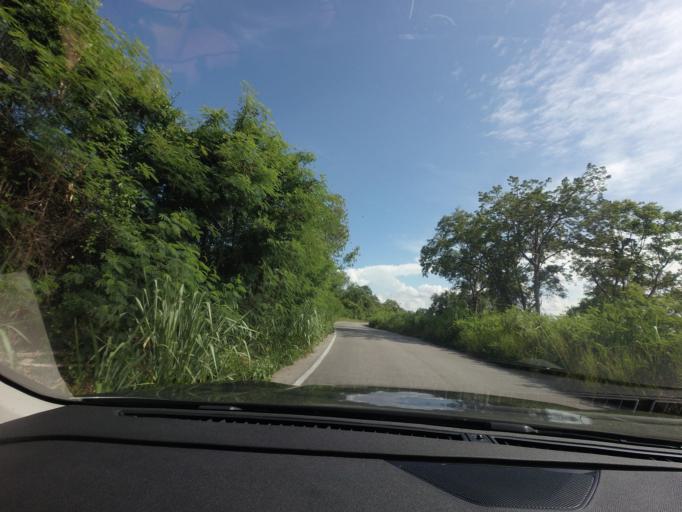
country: TH
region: Prachuap Khiri Khan
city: Hua Hin
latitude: 12.4902
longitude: 99.9426
